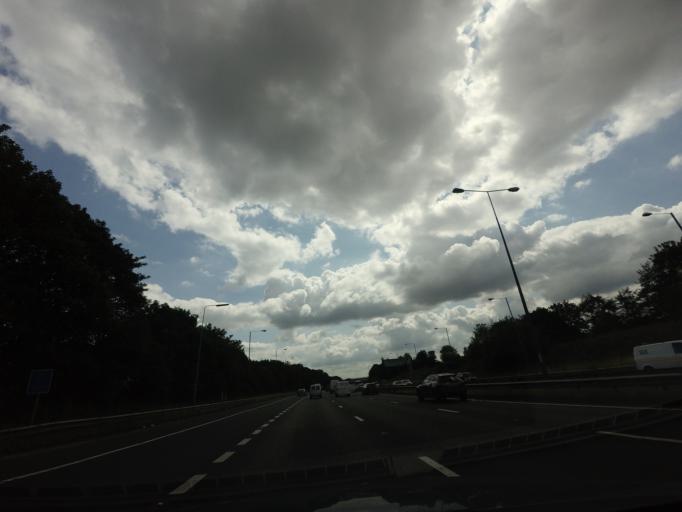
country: GB
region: England
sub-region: Borough of Wigan
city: Ashton in Makerfield
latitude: 53.5042
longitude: -2.6618
